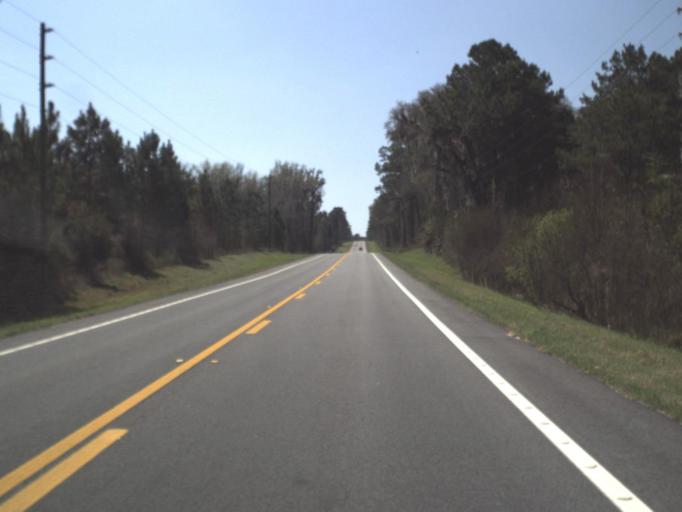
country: US
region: Florida
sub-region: Jefferson County
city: Monticello
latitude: 30.4212
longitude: -84.0202
